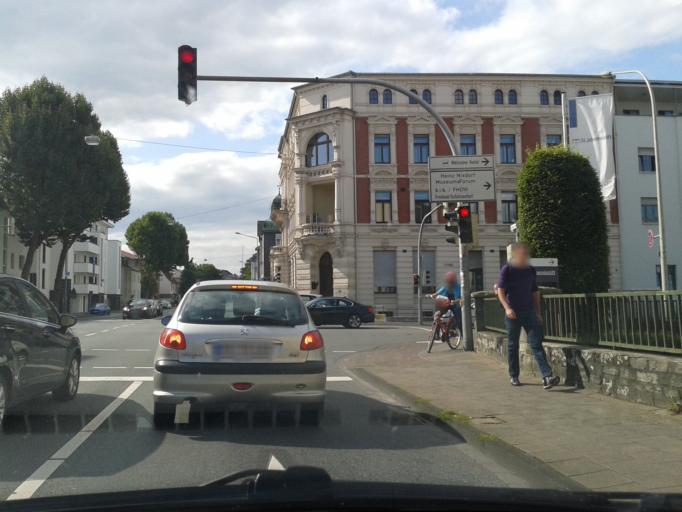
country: DE
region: North Rhine-Westphalia
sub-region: Regierungsbezirk Detmold
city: Paderborn
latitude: 51.7222
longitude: 8.7436
